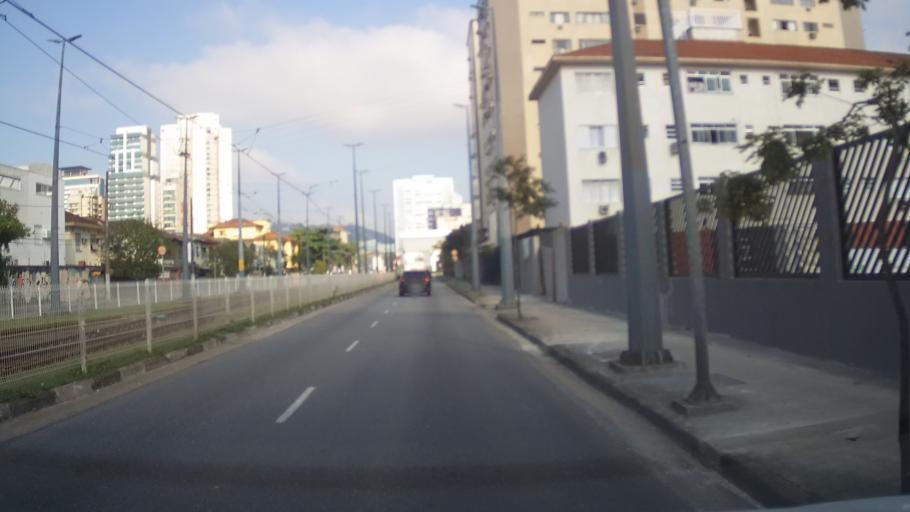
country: BR
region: Sao Paulo
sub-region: Santos
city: Santos
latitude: -23.9575
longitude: -46.3243
